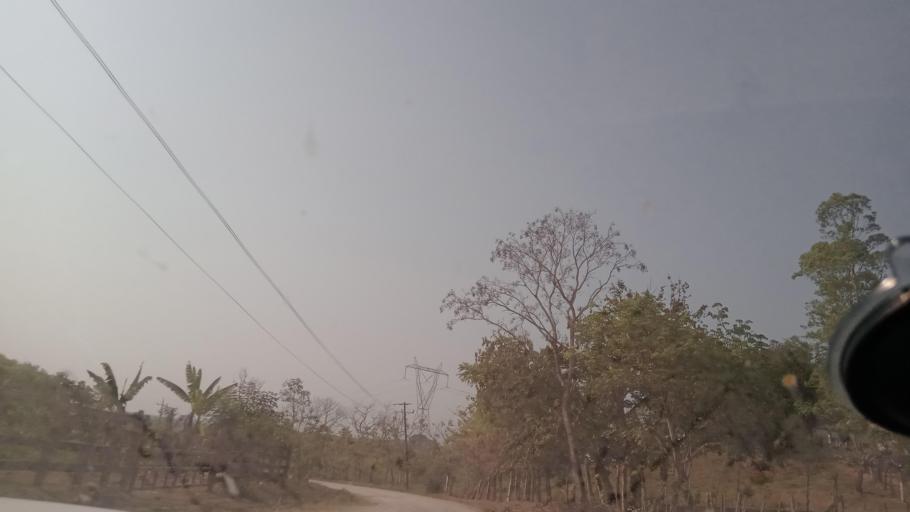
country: MX
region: Tabasco
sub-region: Huimanguillo
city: Francisco Rueda
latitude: 17.6182
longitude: -93.9405
